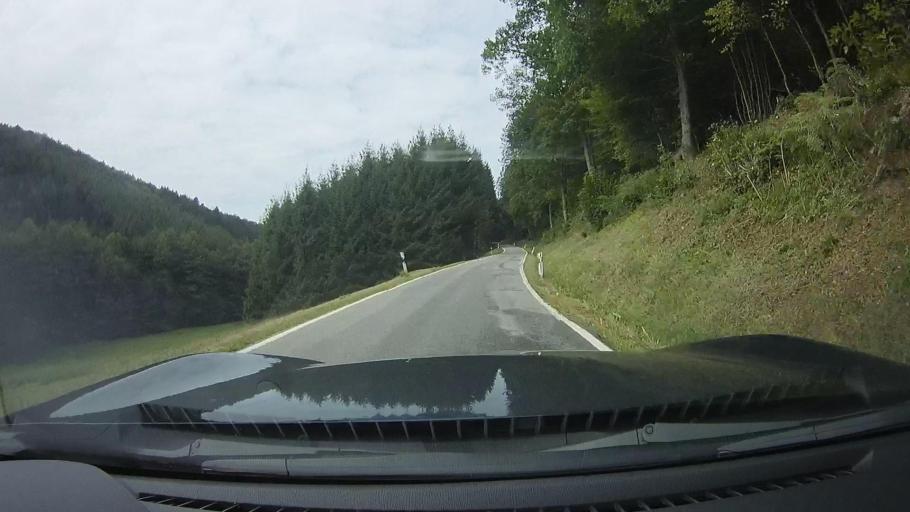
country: DE
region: Baden-Wuerttemberg
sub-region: Regierungsbezirk Stuttgart
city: Lowenstein
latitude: 49.0694
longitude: 9.4211
